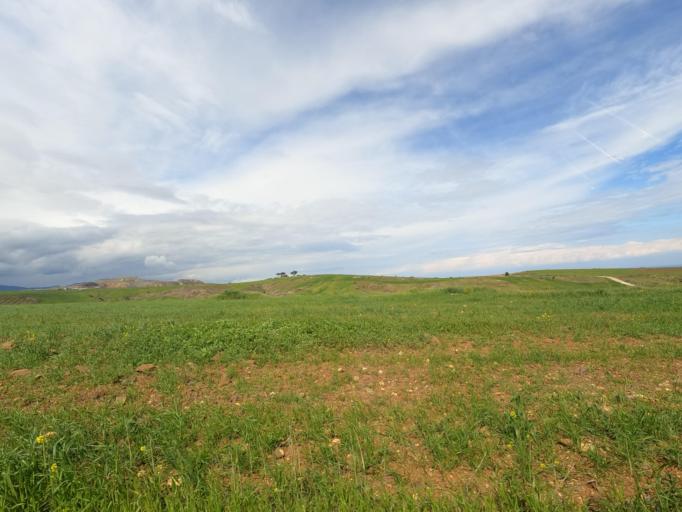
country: CY
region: Lefkosia
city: Lefka
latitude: 35.0931
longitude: 32.9316
